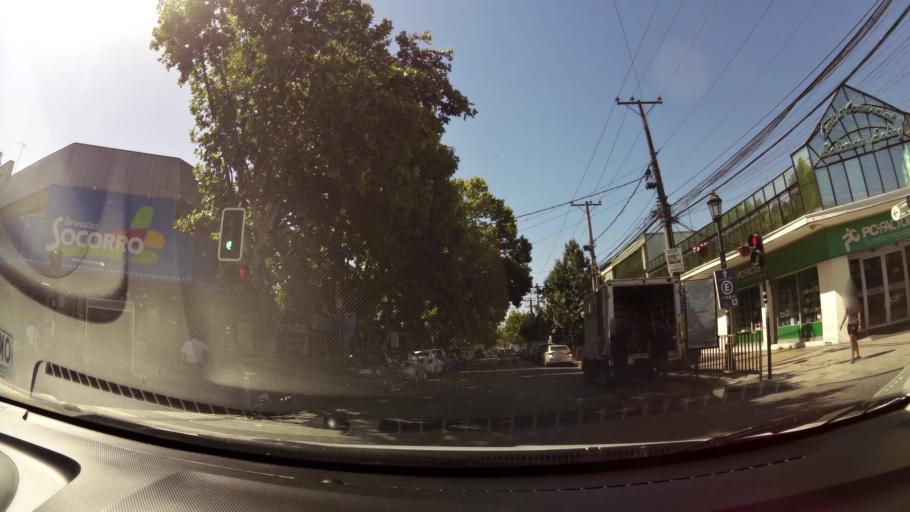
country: CL
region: Maule
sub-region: Provincia de Talca
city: Talca
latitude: -35.4277
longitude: -71.6583
